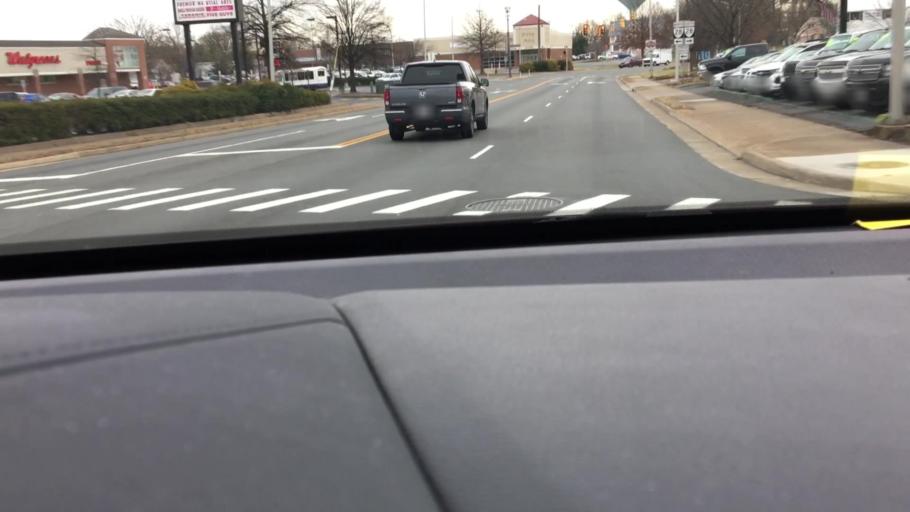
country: US
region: Virginia
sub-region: City of Manassas
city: Manassas
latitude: 38.7562
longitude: -77.4674
